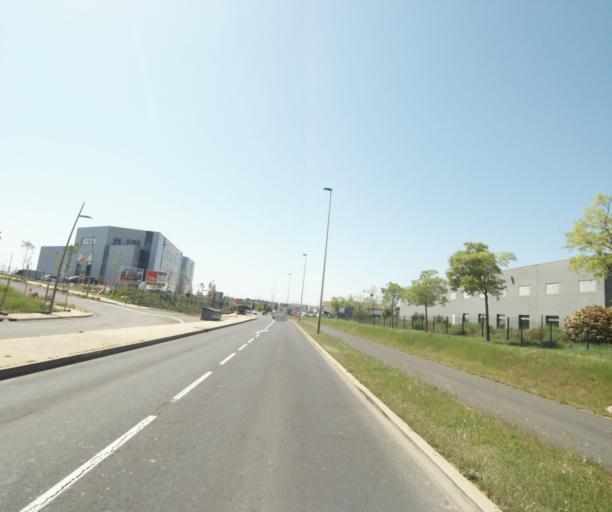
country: FR
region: Languedoc-Roussillon
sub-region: Departement de l'Herault
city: Saint-Jean-de-Vedas
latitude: 43.5753
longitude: 3.8634
